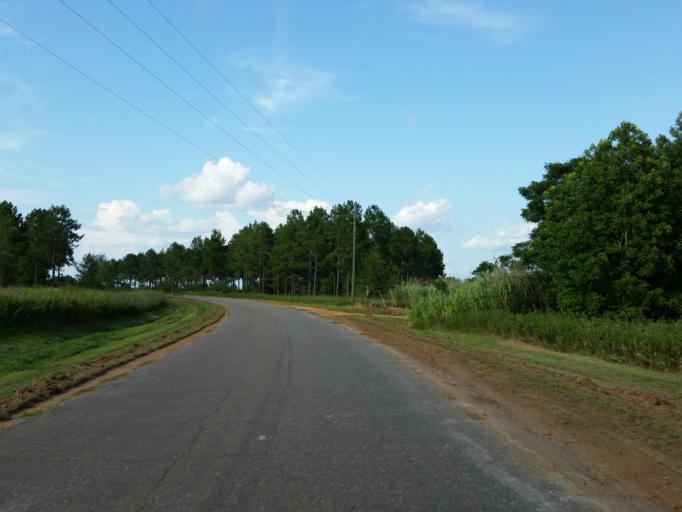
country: US
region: Georgia
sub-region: Crisp County
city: Cordele
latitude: 31.9163
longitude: -84.0125
